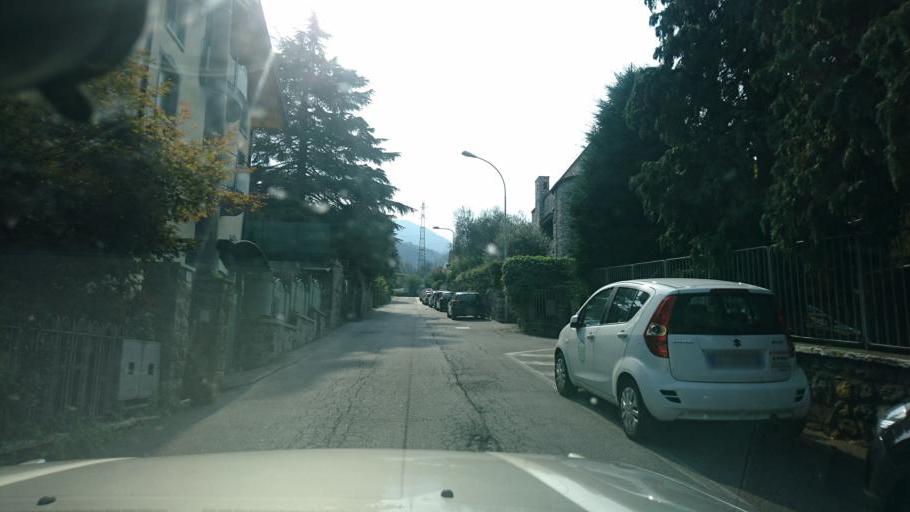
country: IT
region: Lombardy
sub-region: Provincia di Brescia
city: Breno
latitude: 45.9560
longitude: 10.3037
